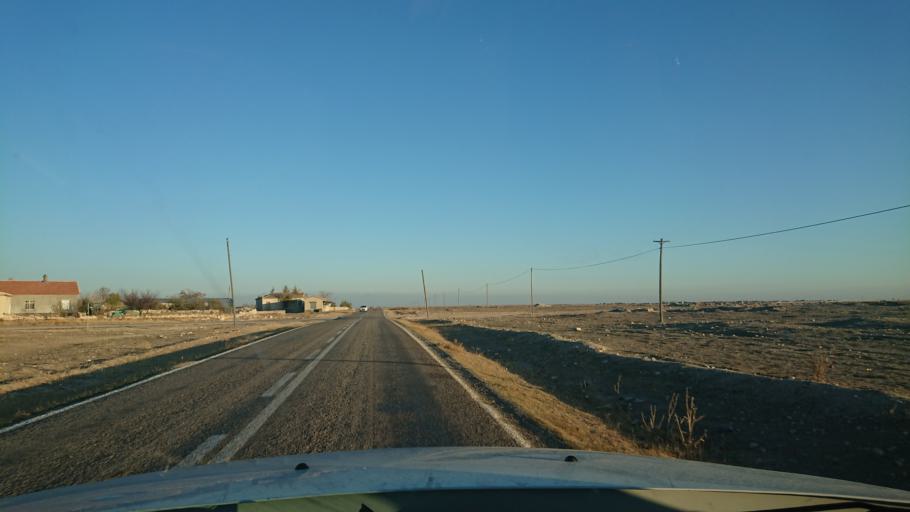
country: TR
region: Aksaray
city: Eskil
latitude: 38.3906
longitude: 33.3234
